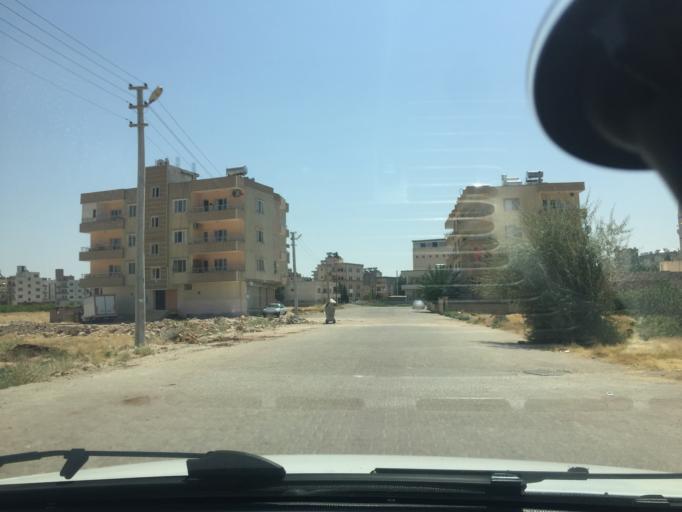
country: TR
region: Mardin
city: Midyat
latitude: 37.4276
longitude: 41.3471
